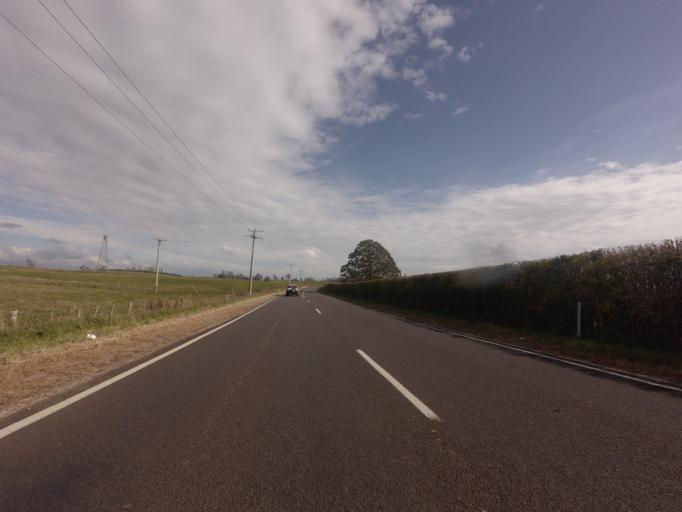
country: AU
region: Tasmania
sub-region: Meander Valley
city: Deloraine
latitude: -41.5237
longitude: 146.7158
